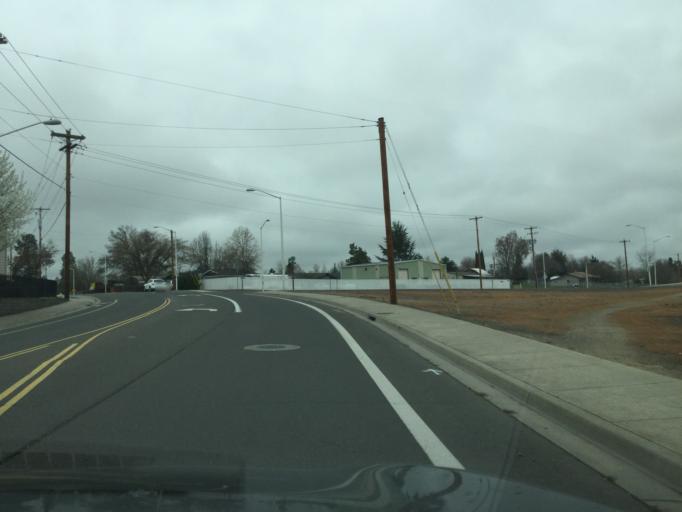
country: US
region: Oregon
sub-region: Jackson County
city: Central Point
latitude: 42.3873
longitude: -122.9200
